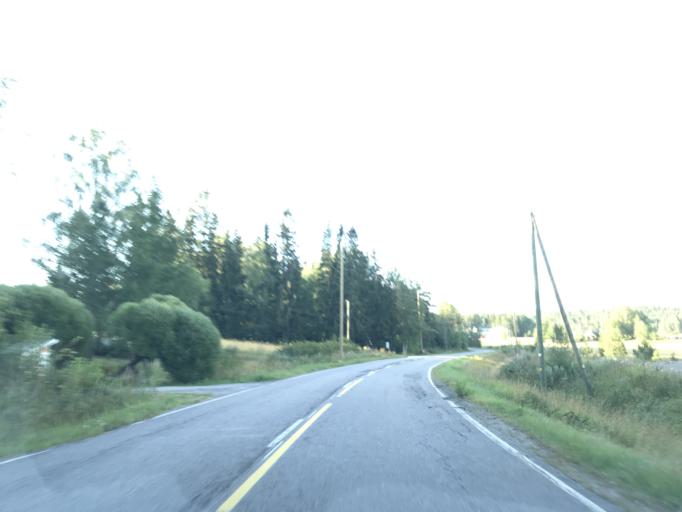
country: FI
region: Uusimaa
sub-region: Helsinki
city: Nurmijaervi
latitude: 60.3668
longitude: 24.6827
